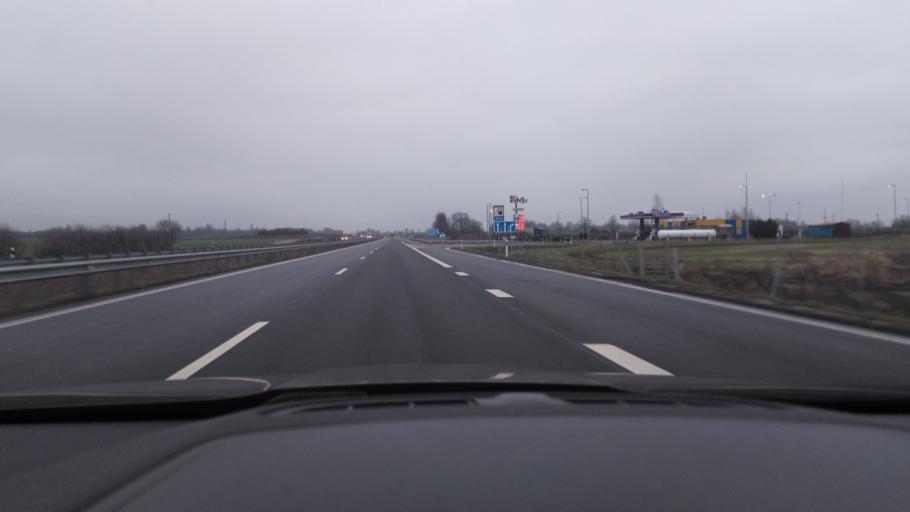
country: LT
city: Kazlu Ruda
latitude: 54.7138
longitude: 23.6473
